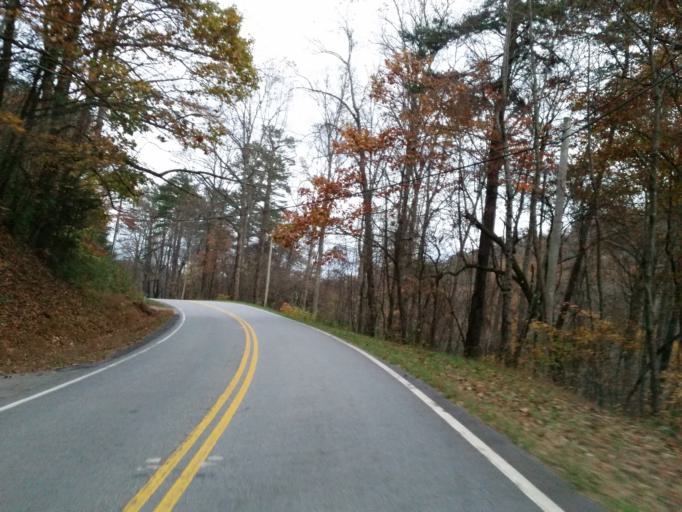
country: US
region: Georgia
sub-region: Union County
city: Blairsville
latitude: 34.7219
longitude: -84.0793
